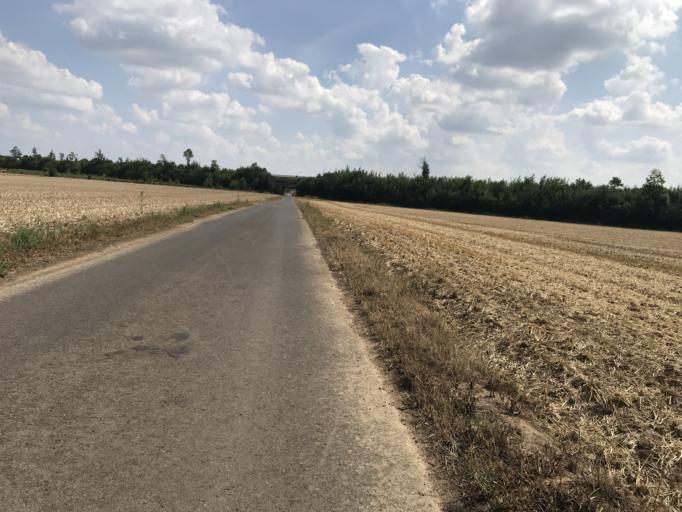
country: DE
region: Hesse
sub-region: Regierungsbezirk Darmstadt
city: Wolfersheim
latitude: 50.4199
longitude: 8.8363
